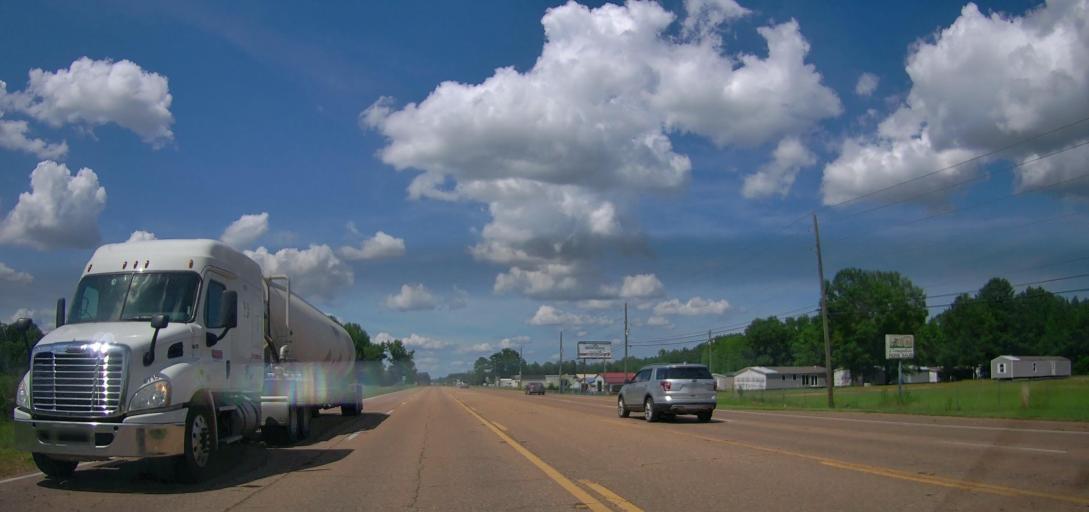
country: US
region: Mississippi
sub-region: Lowndes County
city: Columbus Air Force Base
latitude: 33.5872
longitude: -88.4270
